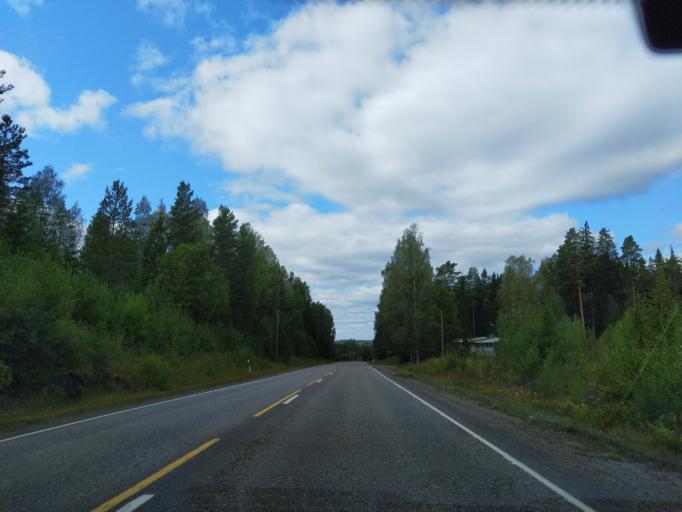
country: FI
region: Haeme
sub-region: Riihimaeki
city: Loppi
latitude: 60.7242
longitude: 24.4204
